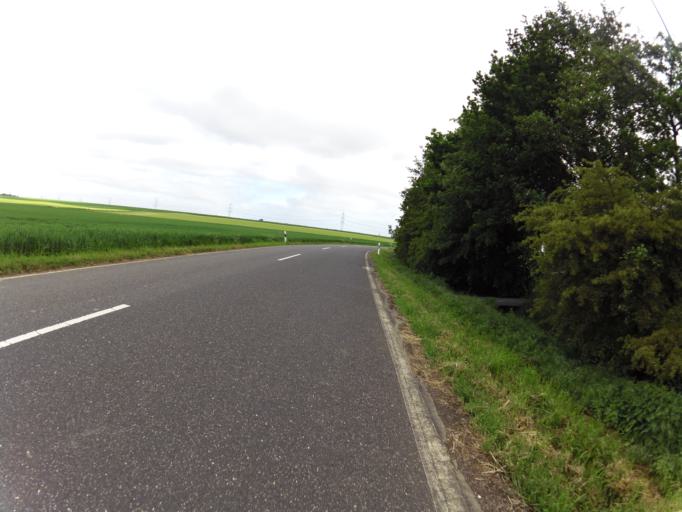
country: DE
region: North Rhine-Westphalia
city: Siersdorf
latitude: 50.9327
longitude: 6.2497
